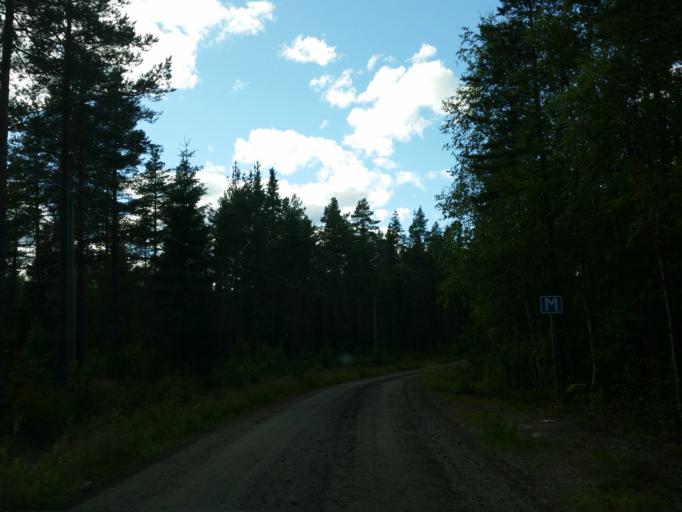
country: SE
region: Vaesterbotten
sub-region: Robertsfors Kommun
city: Robertsfors
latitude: 64.1321
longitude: 20.9476
